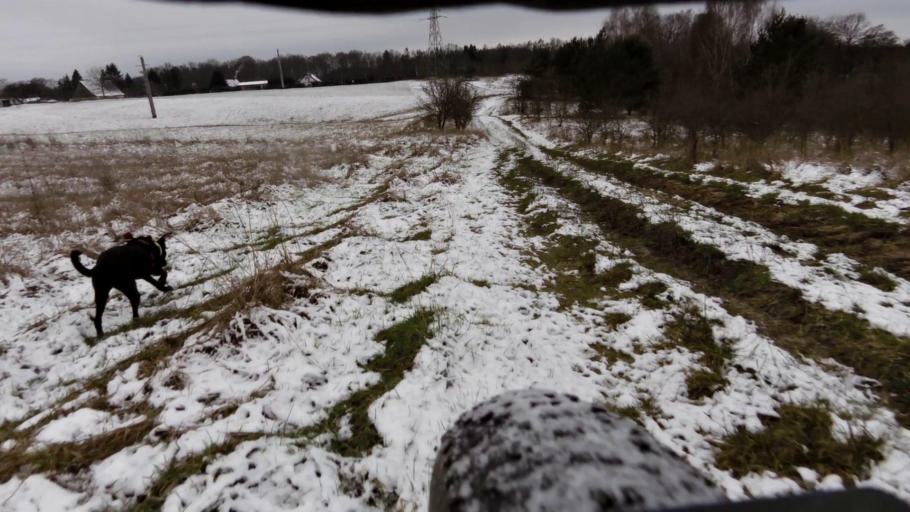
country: PL
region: West Pomeranian Voivodeship
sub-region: Powiat walecki
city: Miroslawiec
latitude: 53.3429
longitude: 16.2678
